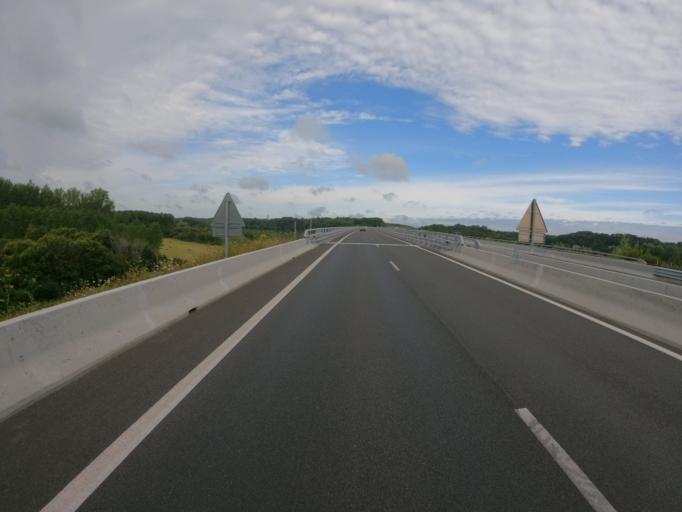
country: FR
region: Centre
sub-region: Departement d'Indre-et-Loire
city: Cinq-Mars-la-Pile
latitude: 47.3347
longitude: 0.4395
